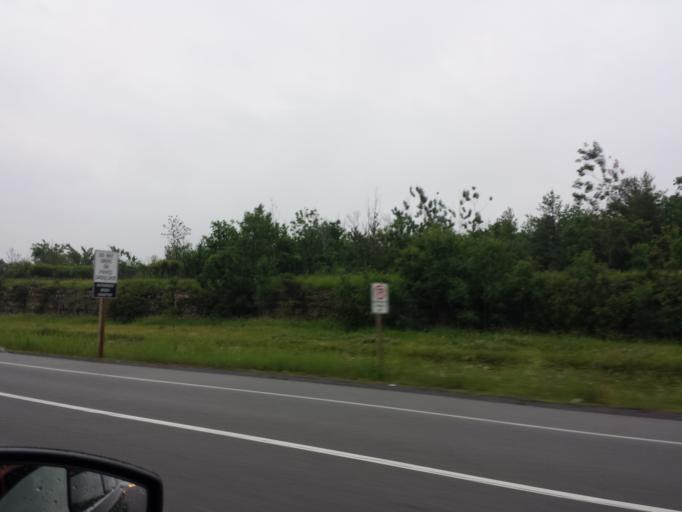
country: CA
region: Ontario
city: Bells Corners
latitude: 45.3278
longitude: -75.8671
